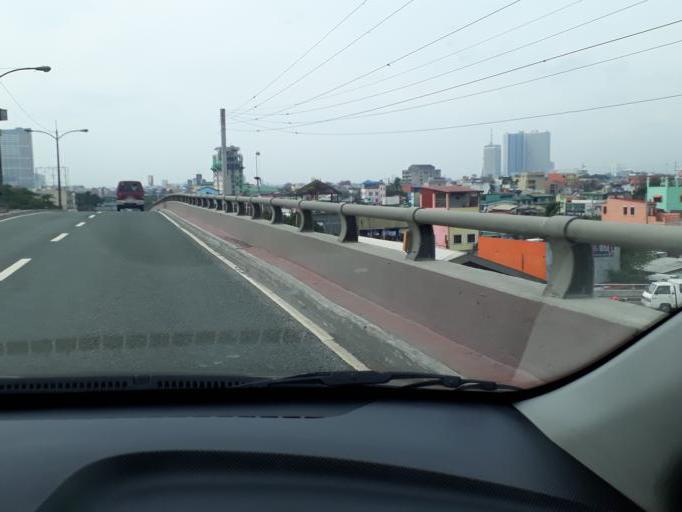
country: PH
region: Metro Manila
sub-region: City of Manila
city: Quiapo
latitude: 14.6007
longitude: 120.9996
